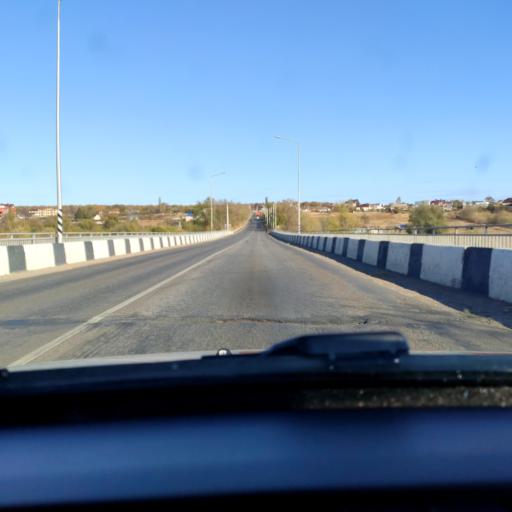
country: RU
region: Voronezj
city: Semiluki
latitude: 51.7264
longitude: 39.0163
